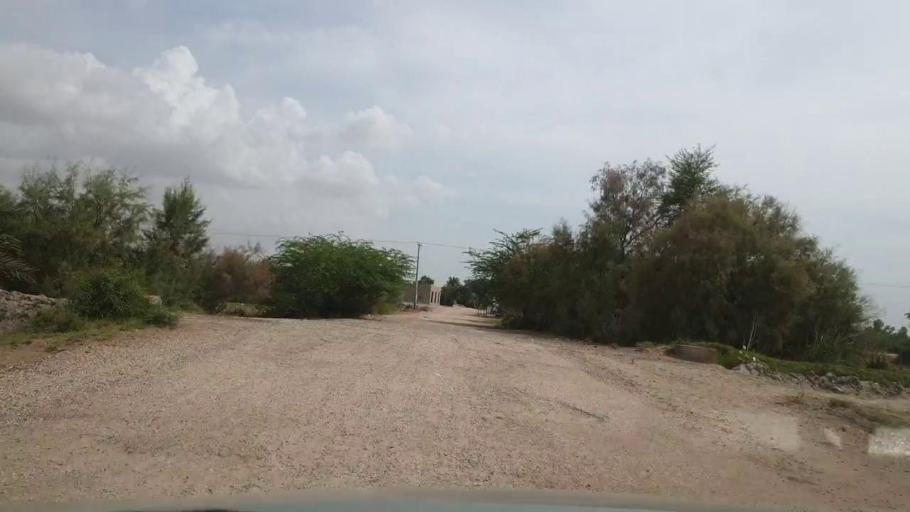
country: PK
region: Sindh
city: Kot Diji
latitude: 27.1112
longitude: 69.0223
